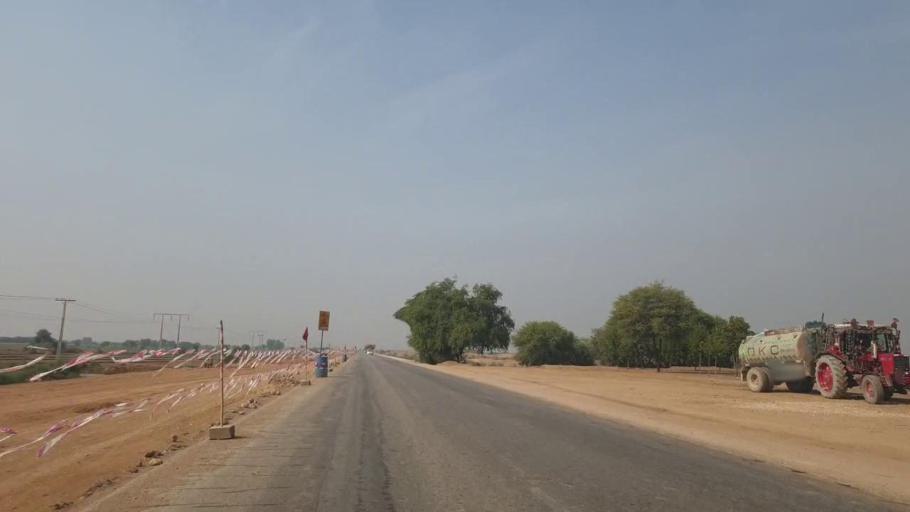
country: PK
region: Sindh
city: Sann
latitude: 26.1342
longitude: 68.0455
